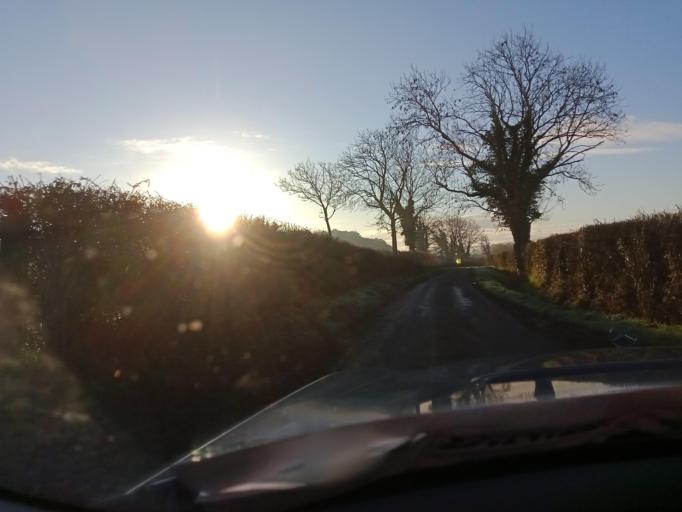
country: IE
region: Leinster
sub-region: Kilkenny
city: Callan
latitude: 52.5362
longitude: -7.4302
